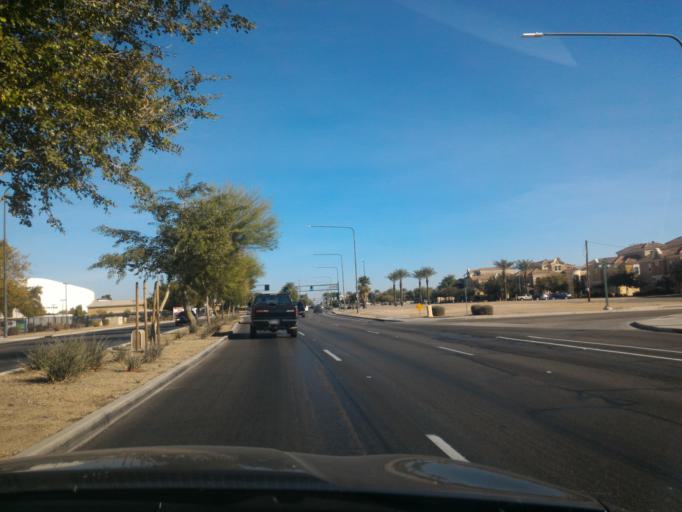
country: US
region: Arizona
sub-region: Maricopa County
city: Chandler
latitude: 33.3060
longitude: -111.8457
